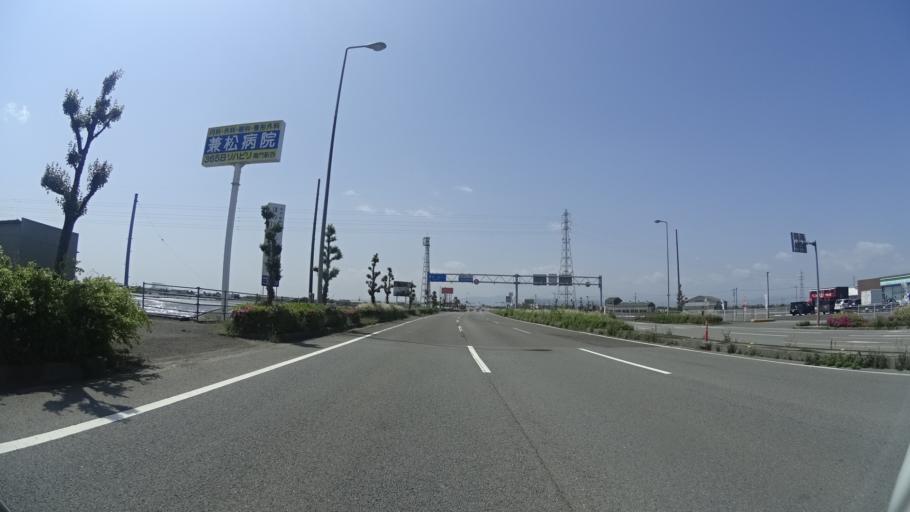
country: JP
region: Tokushima
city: Narutocho-mitsuishi
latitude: 34.1595
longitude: 134.5810
